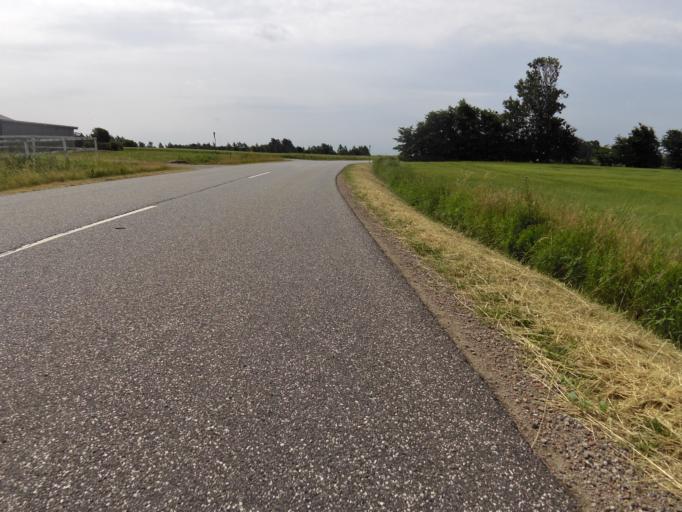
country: DK
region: Central Jutland
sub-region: Holstebro Kommune
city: Holstebro
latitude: 56.4310
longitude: 8.6306
